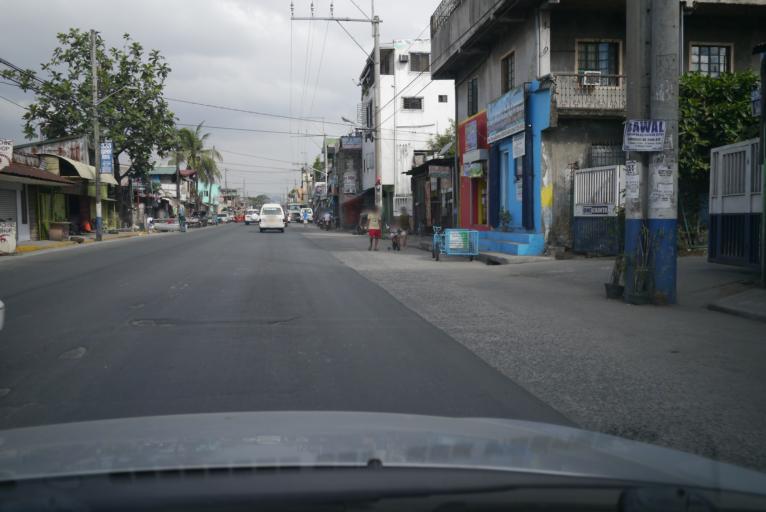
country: PH
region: Calabarzon
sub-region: Province of Rizal
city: Cainta
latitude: 14.5714
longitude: 121.1050
